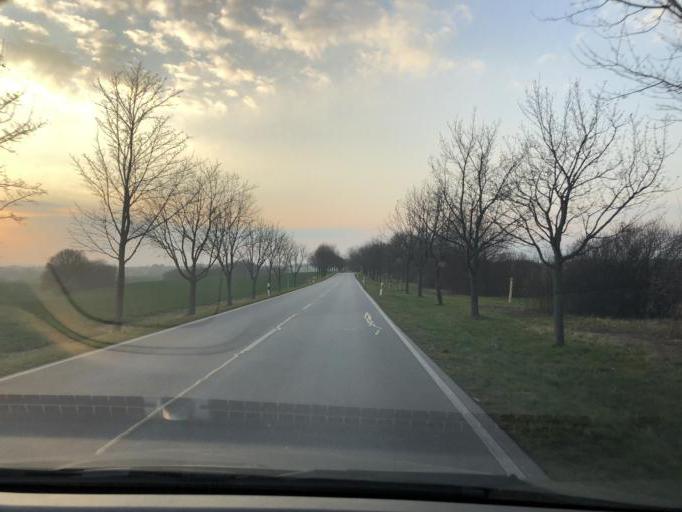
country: DE
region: Saxony
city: Goda
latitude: 51.1998
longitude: 14.3172
